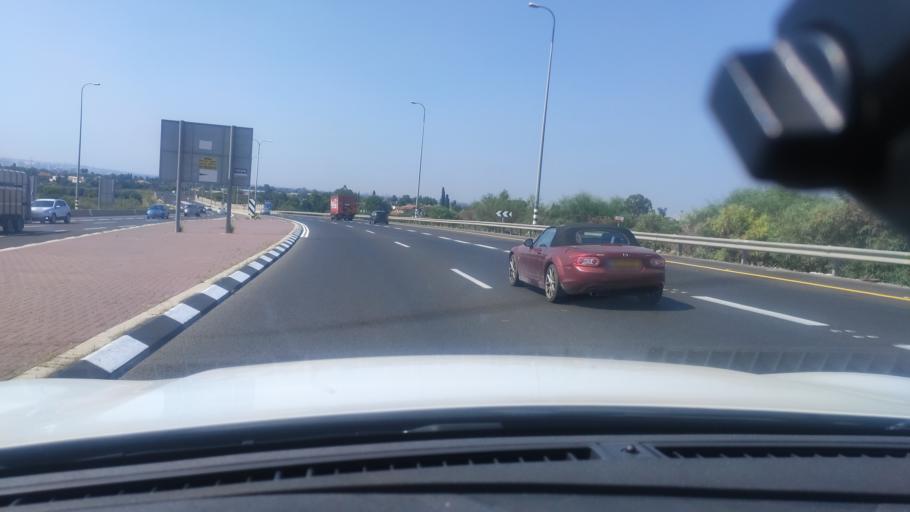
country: IL
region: Central District
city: Kfar Saba
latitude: 32.1631
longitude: 34.9258
